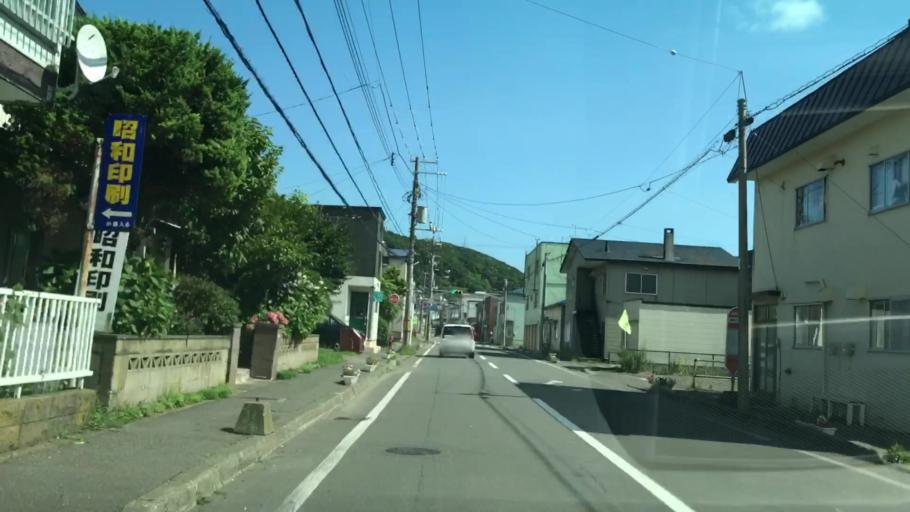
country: JP
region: Hokkaido
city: Muroran
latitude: 42.3117
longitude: 140.9939
